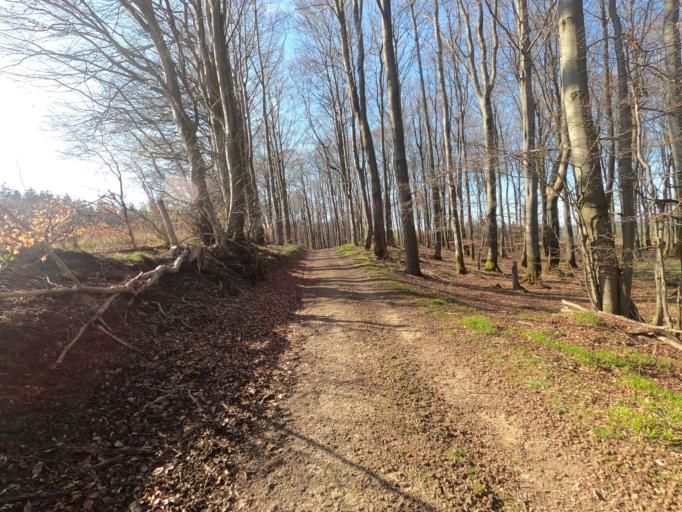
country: DE
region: North Rhine-Westphalia
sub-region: Regierungsbezirk Arnsberg
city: Herscheid
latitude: 51.1712
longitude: 7.7129
